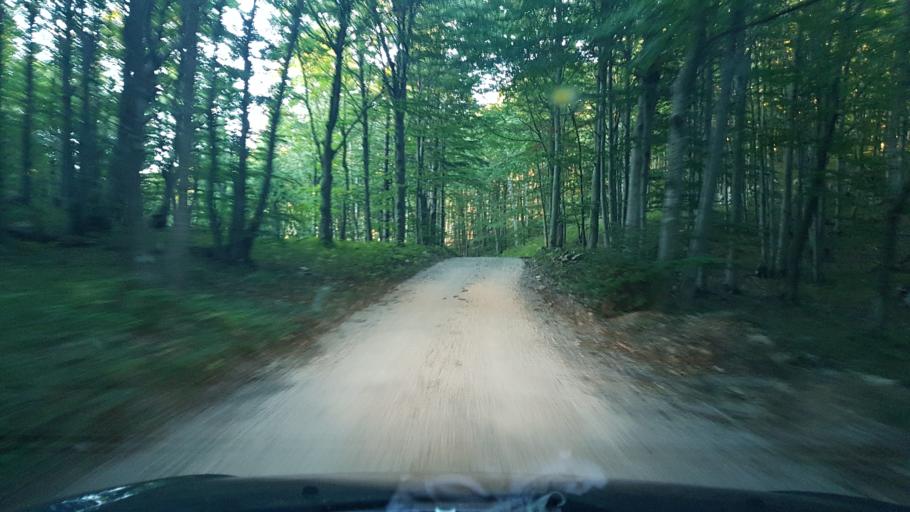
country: SI
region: Vipava
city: Vipava
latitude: 45.7742
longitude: 14.0492
